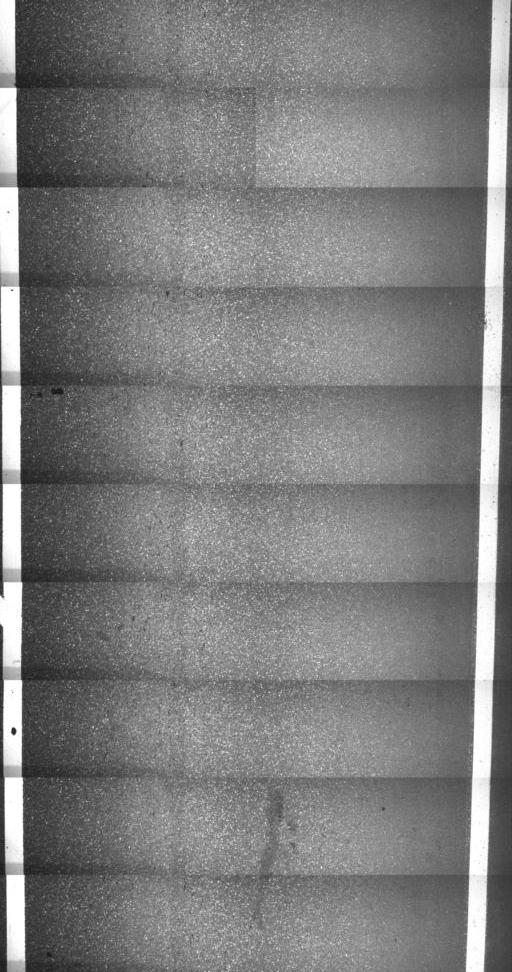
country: US
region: Vermont
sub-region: Washington County
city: Montpelier
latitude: 44.2216
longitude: -72.5582
